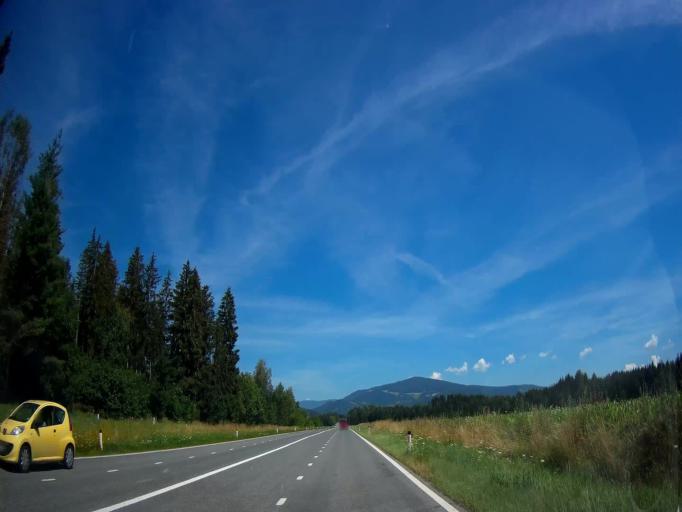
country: AT
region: Carinthia
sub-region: Politischer Bezirk Sankt Veit an der Glan
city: Molbling
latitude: 46.8465
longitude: 14.4480
